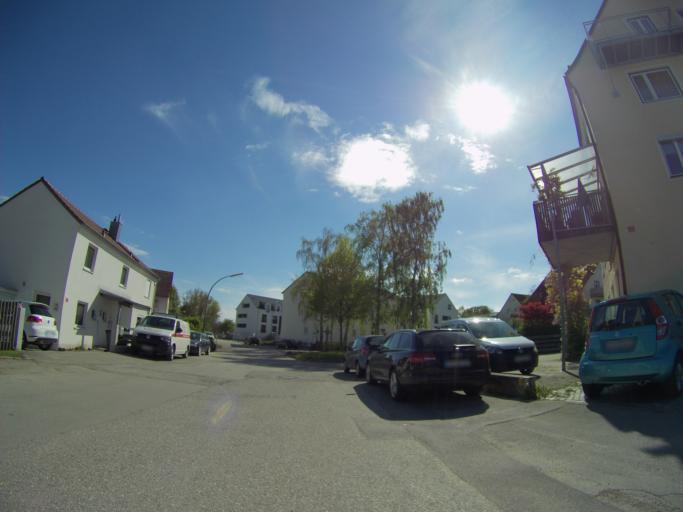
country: DE
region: Bavaria
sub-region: Upper Bavaria
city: Freising
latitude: 48.4087
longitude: 11.7689
